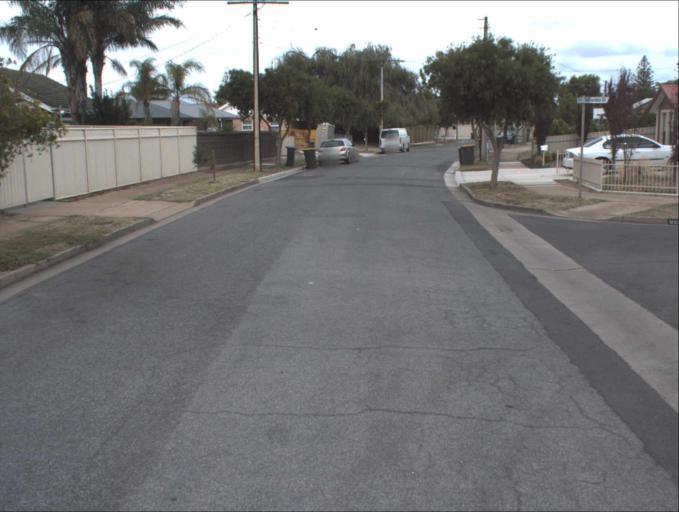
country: AU
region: South Australia
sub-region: Port Adelaide Enfield
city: Birkenhead
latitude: -34.8156
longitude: 138.5048
